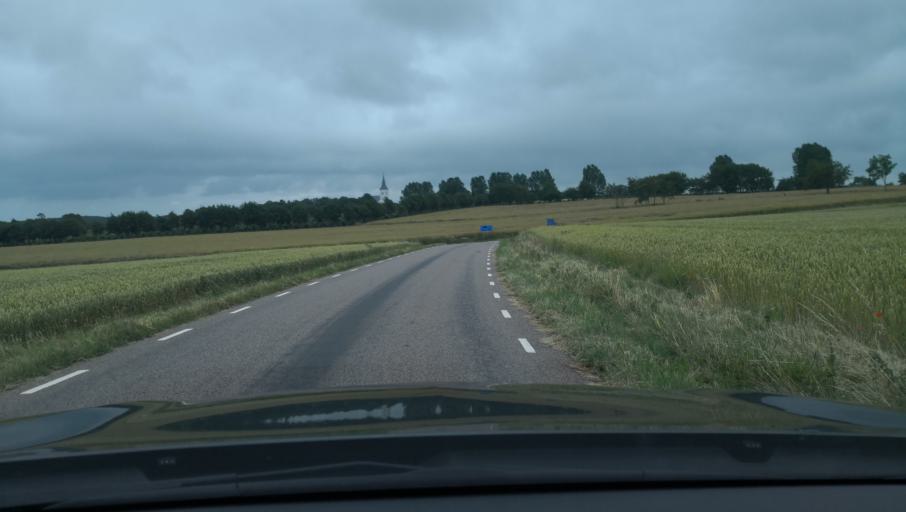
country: SE
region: Skane
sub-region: Simrishamns Kommun
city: Kivik
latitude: 55.6690
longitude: 14.2094
